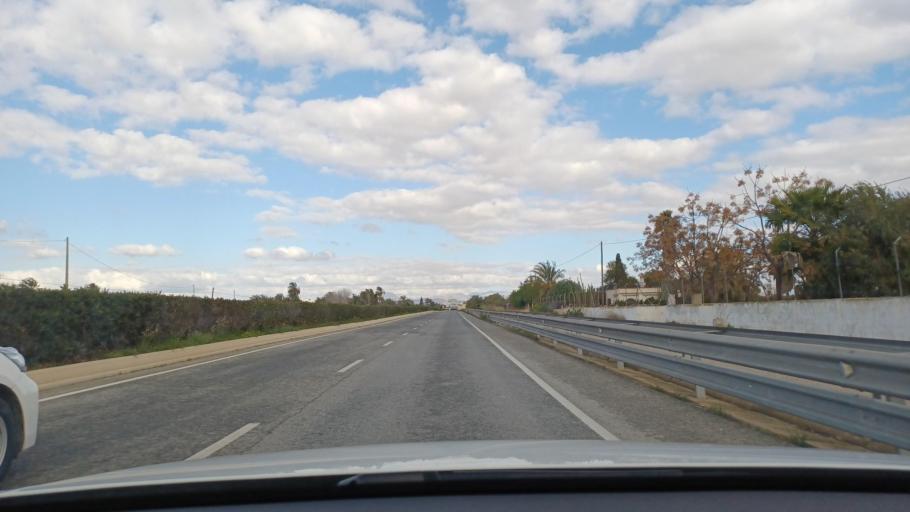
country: ES
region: Valencia
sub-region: Provincia de Alicante
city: Elche
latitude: 38.1816
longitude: -0.7016
